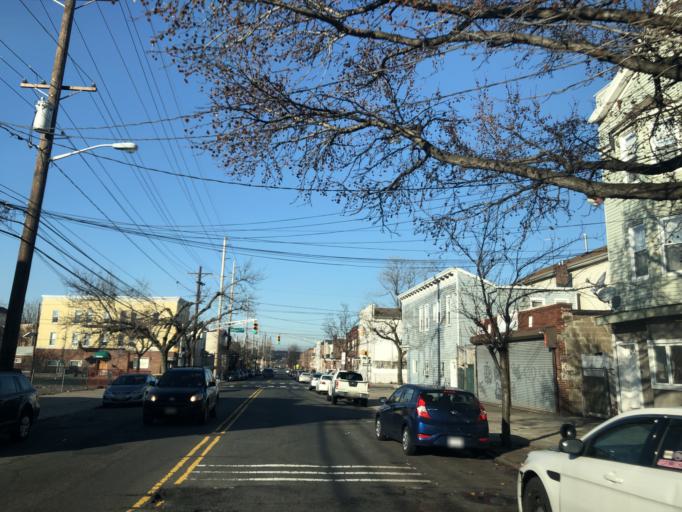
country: US
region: New Jersey
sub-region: Hudson County
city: Jersey City
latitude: 40.7329
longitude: -74.0745
